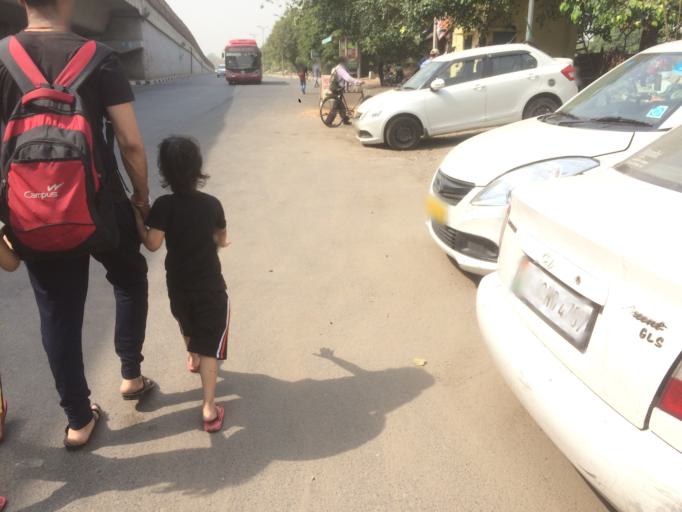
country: IN
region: NCT
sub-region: Central Delhi
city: Karol Bagh
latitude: 28.6190
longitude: 77.1362
